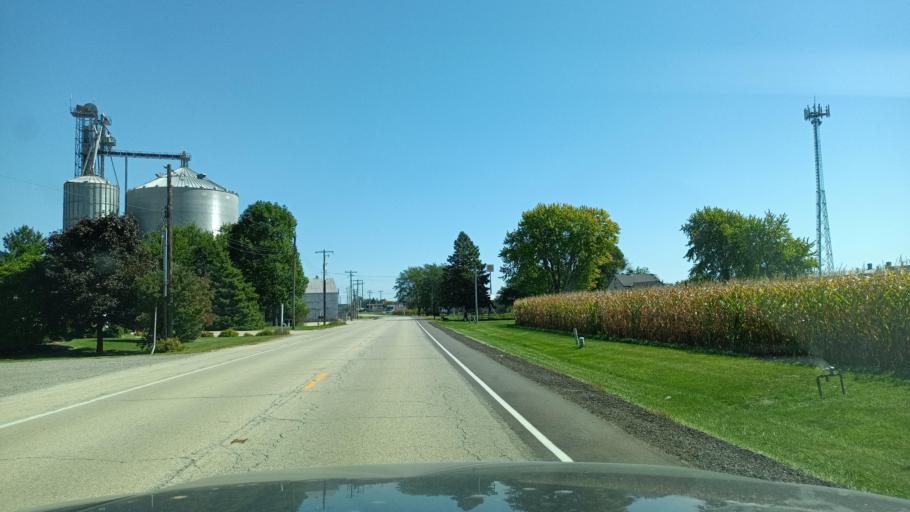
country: US
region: Illinois
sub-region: Woodford County
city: Eureka
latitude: 40.6280
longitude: -89.2813
